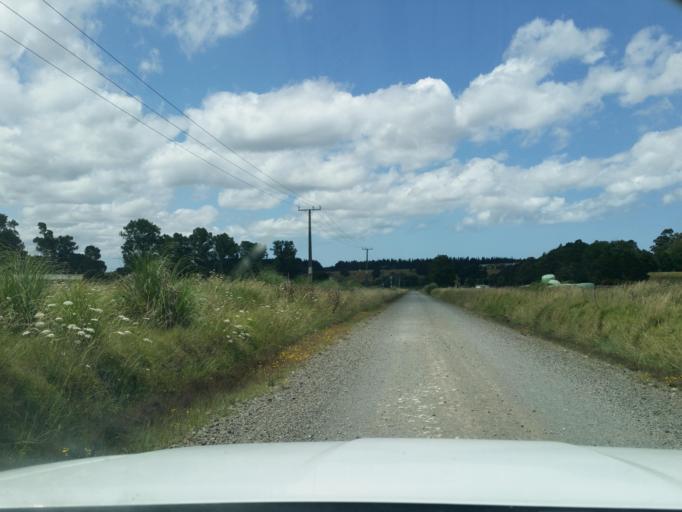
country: NZ
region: Northland
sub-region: Kaipara District
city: Dargaville
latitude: -35.8027
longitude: 173.7312
